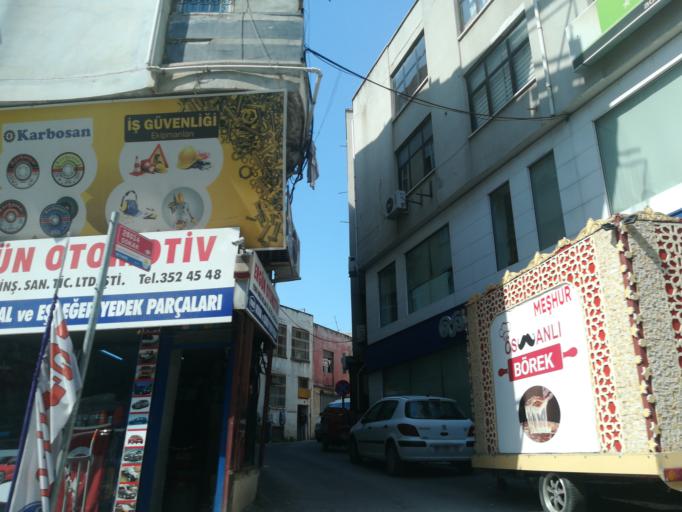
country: TR
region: Adana
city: Adana
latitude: 36.9851
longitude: 35.3291
